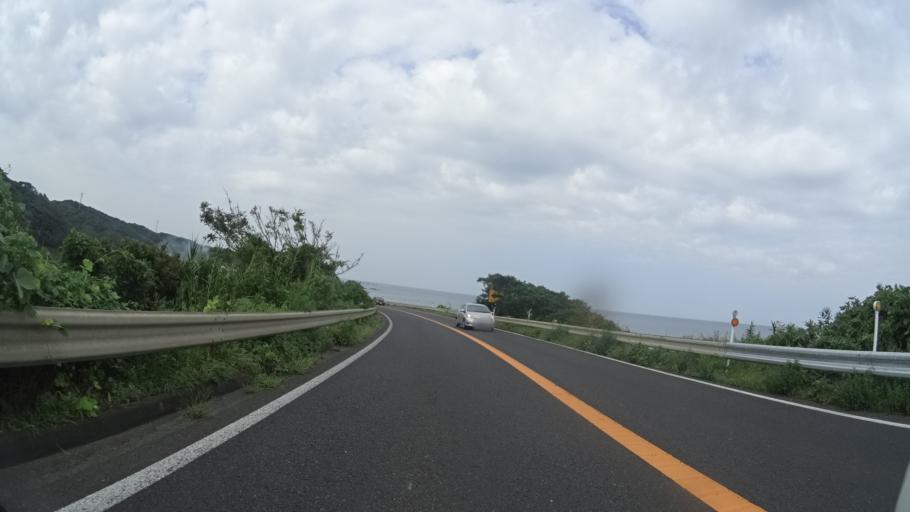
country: JP
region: Shimane
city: Odacho-oda
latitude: 35.1964
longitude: 132.4482
